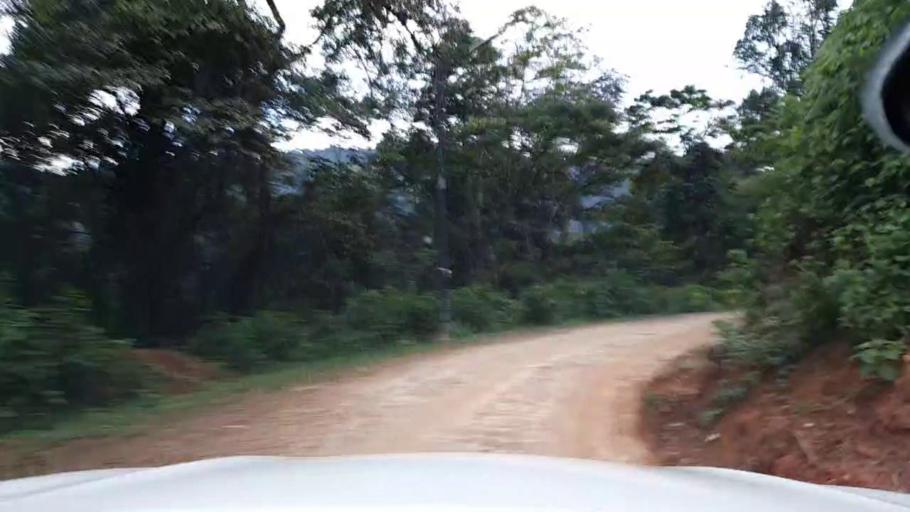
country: RW
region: Western Province
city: Cyangugu
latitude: -2.5597
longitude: 29.2285
